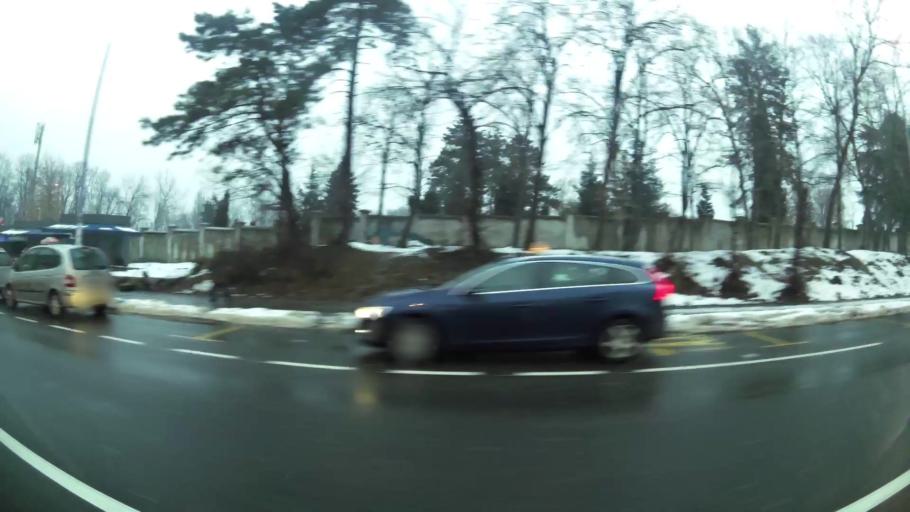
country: RS
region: Central Serbia
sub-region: Belgrade
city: Vozdovac
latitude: 44.7745
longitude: 20.4917
